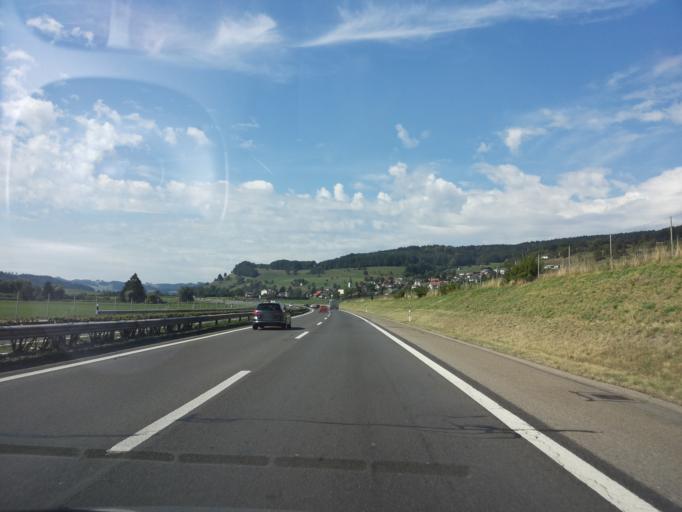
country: CH
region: Lucerne
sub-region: Willisau District
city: Wauwil
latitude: 47.2067
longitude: 8.0332
